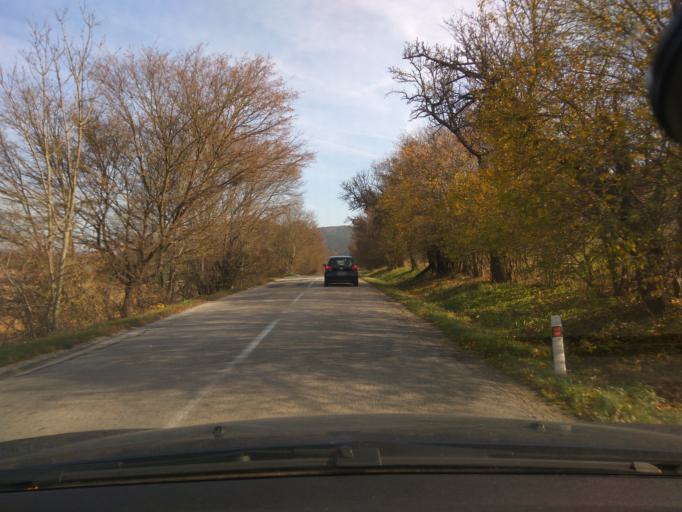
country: SK
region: Nitriansky
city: Brezova pod Bradlom
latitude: 48.6524
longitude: 17.5150
